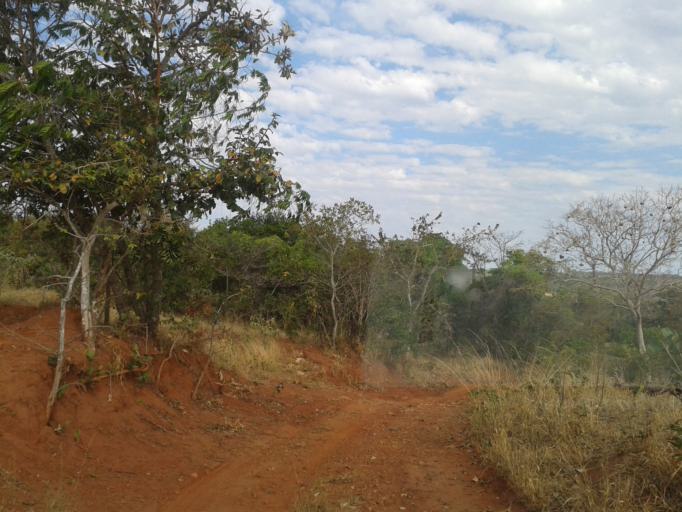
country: BR
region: Minas Gerais
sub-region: Ituiutaba
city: Ituiutaba
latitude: -19.0258
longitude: -49.2107
